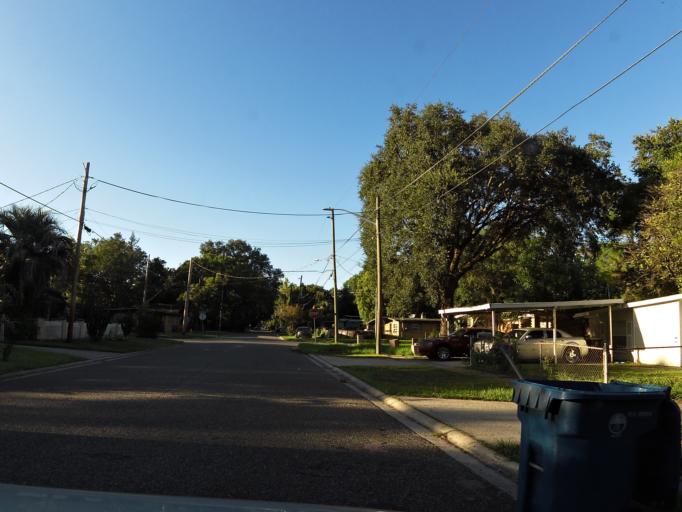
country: US
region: Florida
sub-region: Duval County
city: Jacksonville
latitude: 30.3575
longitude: -81.7006
